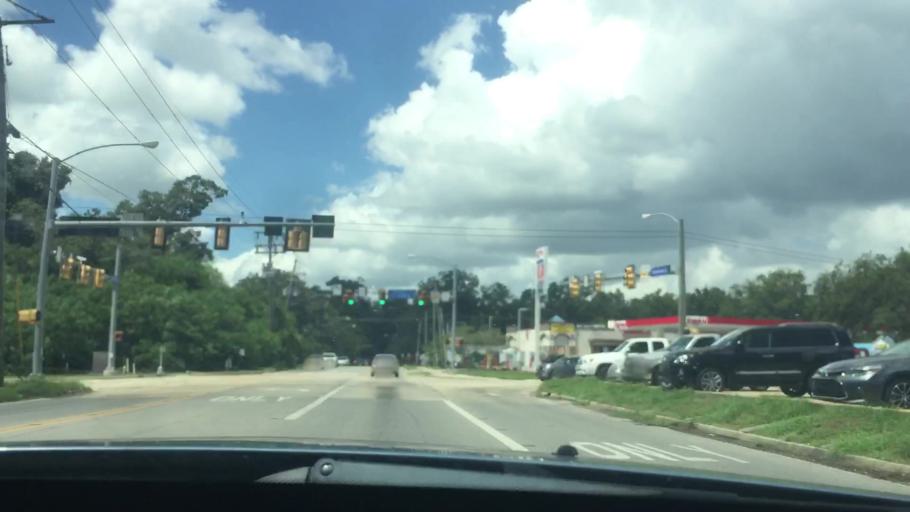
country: US
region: Louisiana
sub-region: East Baton Rouge Parish
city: Gardere
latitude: 30.3678
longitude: -91.1213
